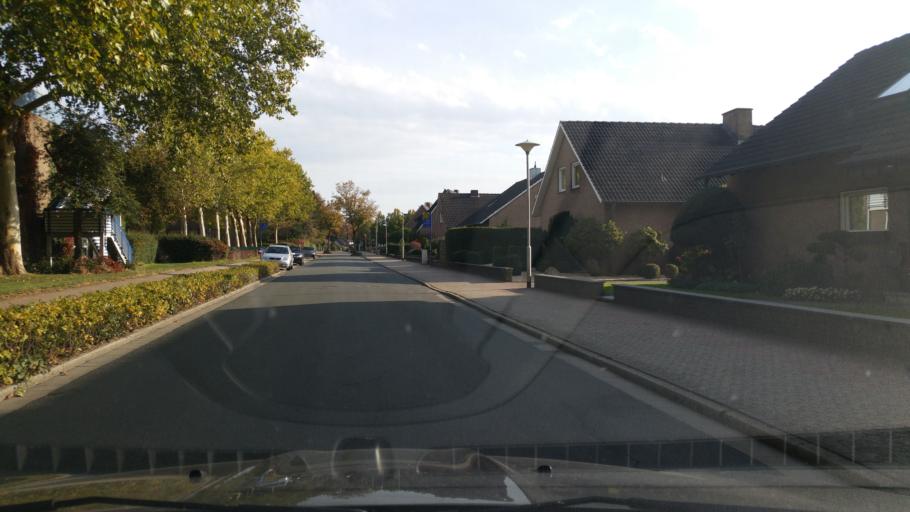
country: DE
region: North Rhine-Westphalia
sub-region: Regierungsbezirk Dusseldorf
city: Bocholt
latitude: 51.8391
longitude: 6.5715
